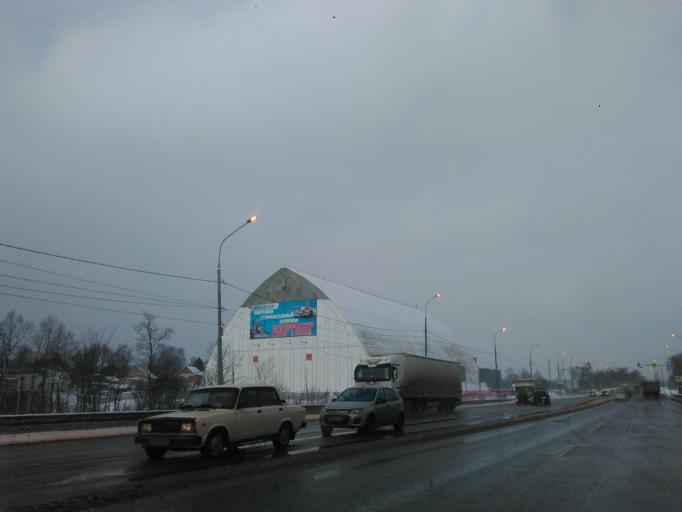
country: RU
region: Moskovskaya
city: Podosinki
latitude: 56.2074
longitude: 37.5231
